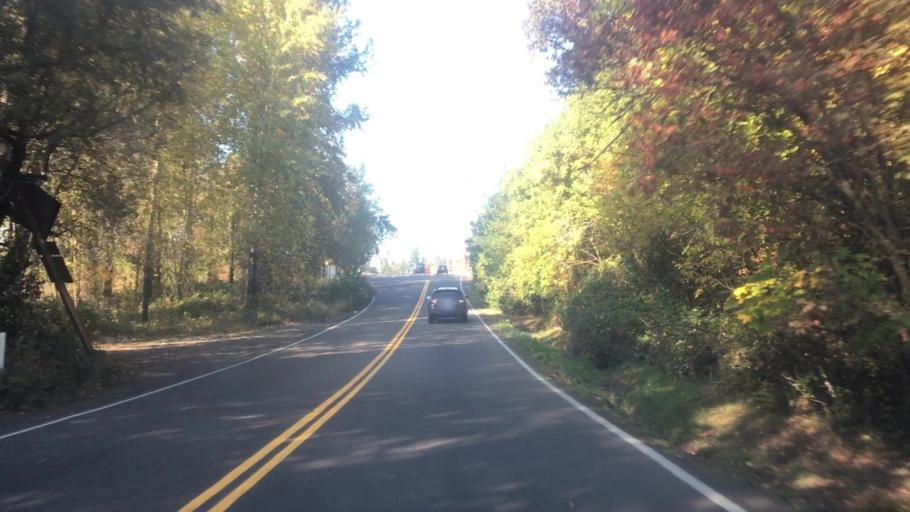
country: US
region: Oregon
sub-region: Washington County
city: Metzger
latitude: 45.4380
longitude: -122.7512
